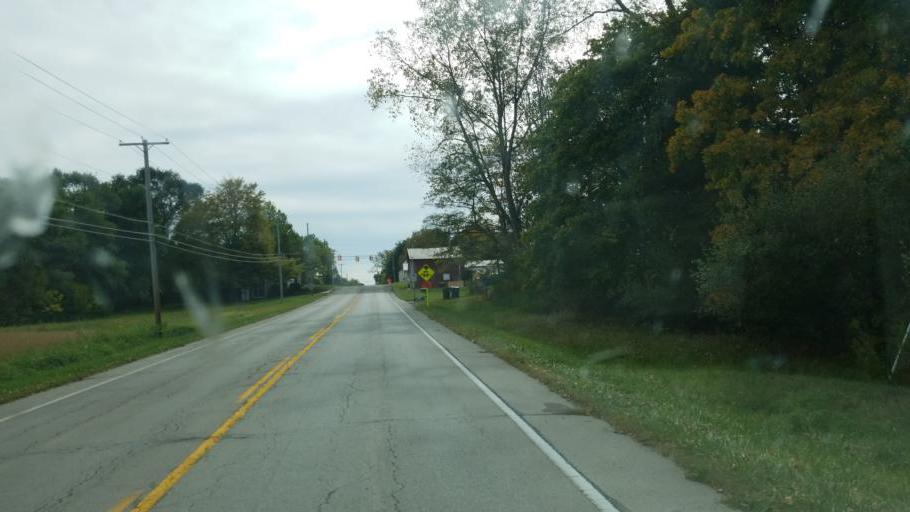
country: US
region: Ohio
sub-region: Lorain County
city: South Amherst
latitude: 41.3904
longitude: -82.2825
